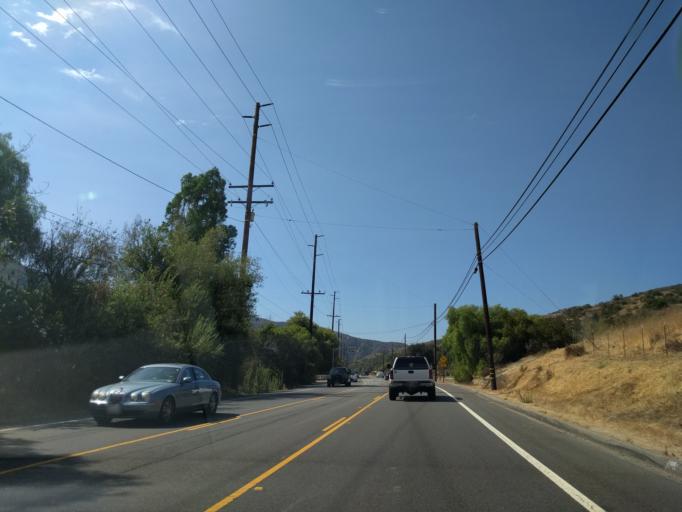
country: US
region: California
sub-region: Orange County
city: Aliso Viejo
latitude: 33.5811
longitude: -117.7616
